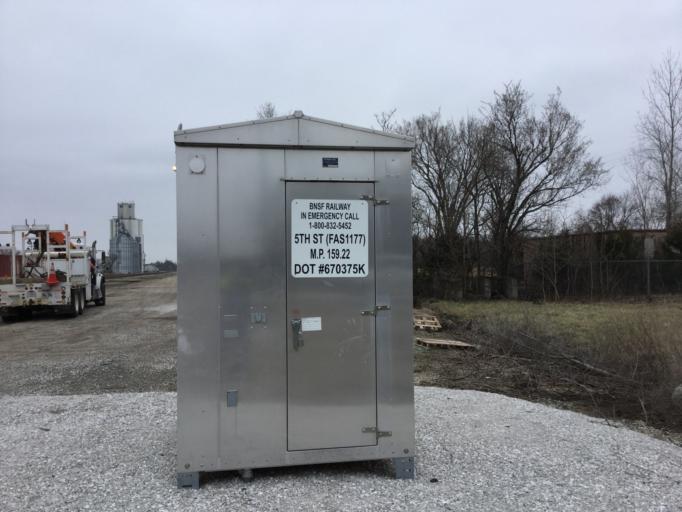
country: US
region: Kansas
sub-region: Cherokee County
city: Baxter Springs
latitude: 37.0309
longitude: -94.7445
